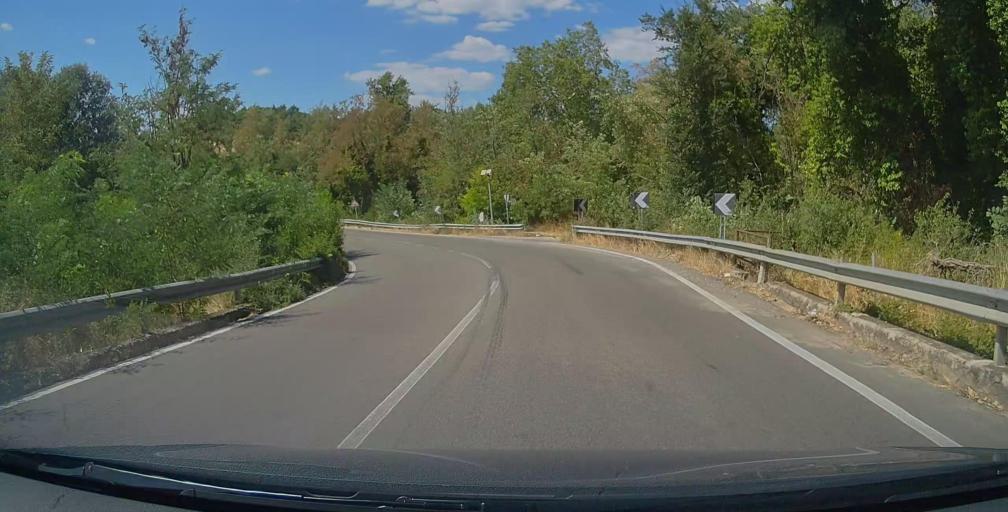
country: IT
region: Umbria
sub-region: Provincia di Terni
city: Otricoli
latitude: 42.3920
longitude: 12.4689
